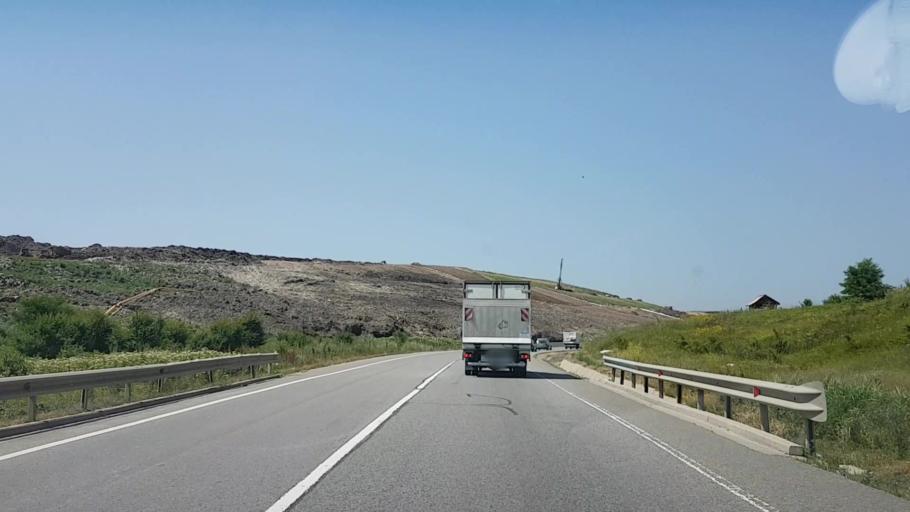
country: RO
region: Cluj
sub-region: Comuna Apahida
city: Dezmir
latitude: 46.7626
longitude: 23.6912
